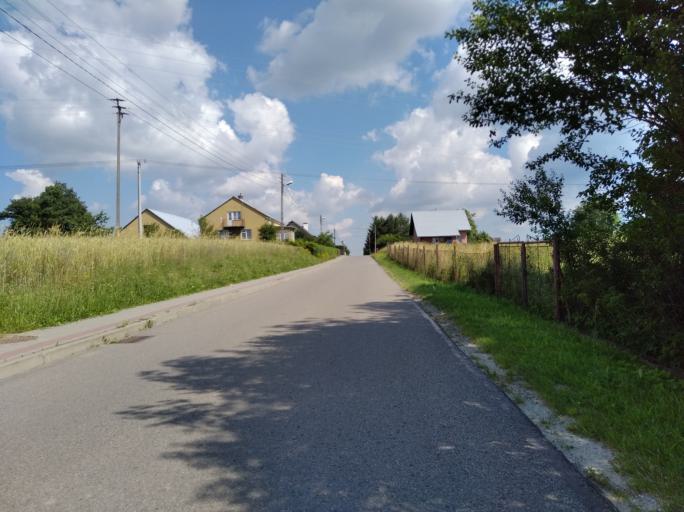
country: PL
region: Subcarpathian Voivodeship
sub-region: Powiat rzeszowski
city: Dynow
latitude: 49.8238
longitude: 22.2277
